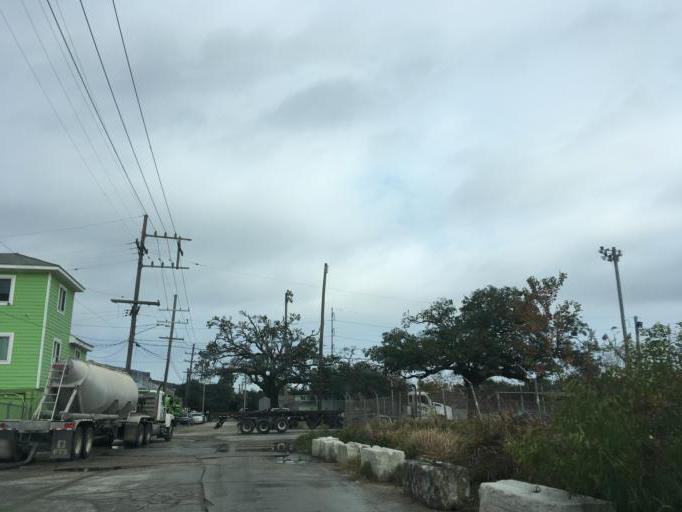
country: US
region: Louisiana
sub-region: Orleans Parish
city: New Orleans
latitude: 29.9872
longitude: -90.0619
